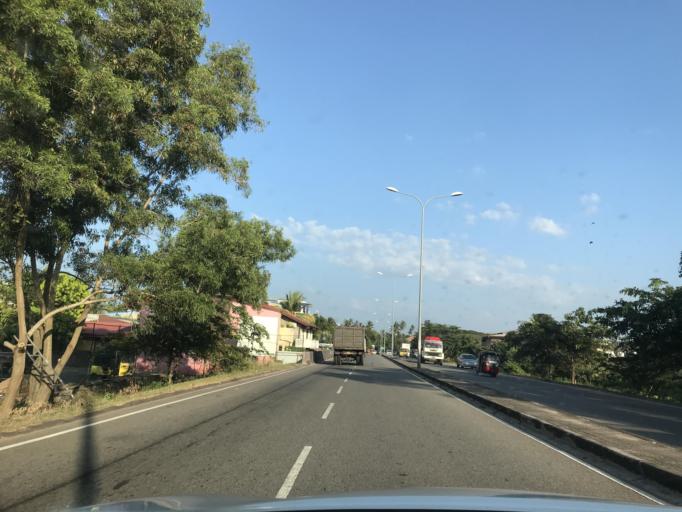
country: LK
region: Western
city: Ja Ela
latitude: 7.0823
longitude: 79.8872
